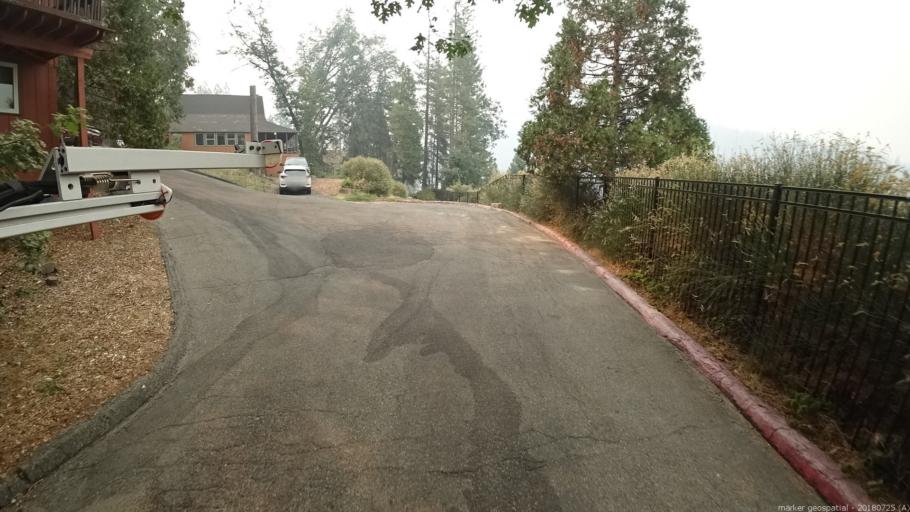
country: US
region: California
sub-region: Madera County
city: Oakhurst
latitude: 37.3185
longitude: -119.5565
